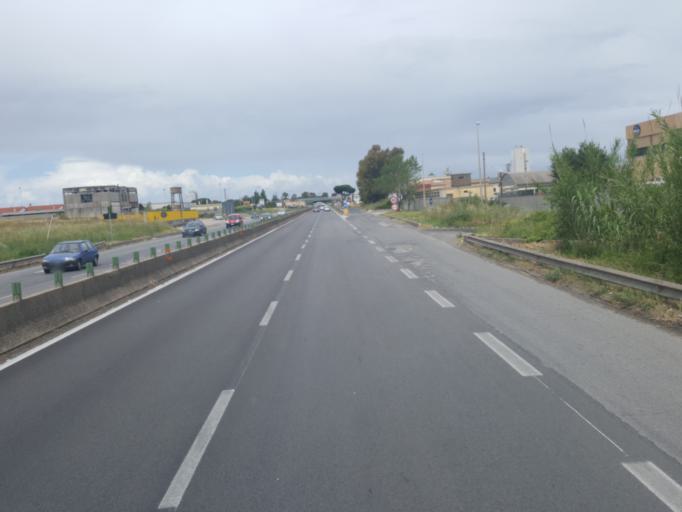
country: IT
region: Latium
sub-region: Provincia di Latina
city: Aprilia
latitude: 41.5734
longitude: 12.6615
